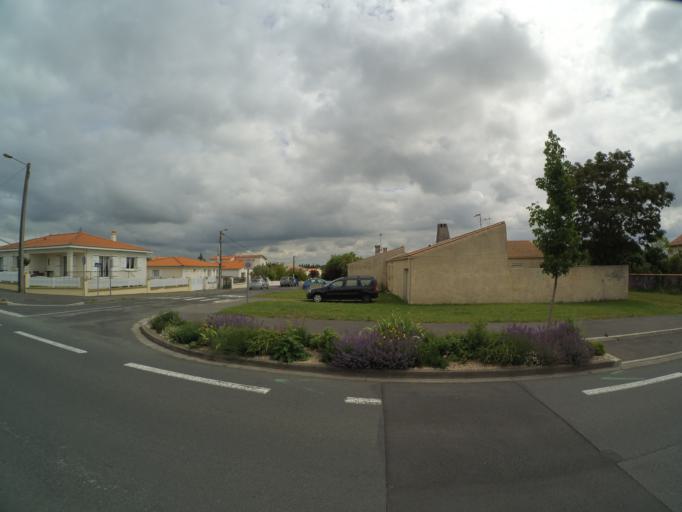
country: FR
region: Poitou-Charentes
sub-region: Departement de la Charente-Maritime
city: Rochefort
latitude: 45.9513
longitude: -0.9679
